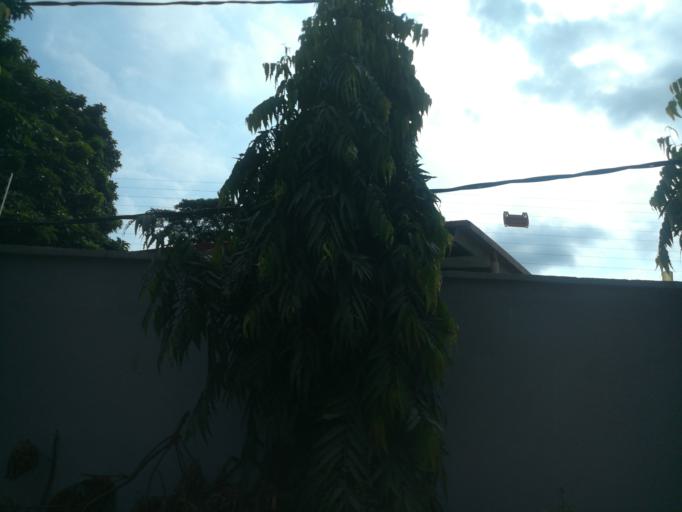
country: NG
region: Lagos
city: Oshodi
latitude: 6.5763
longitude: 3.3557
